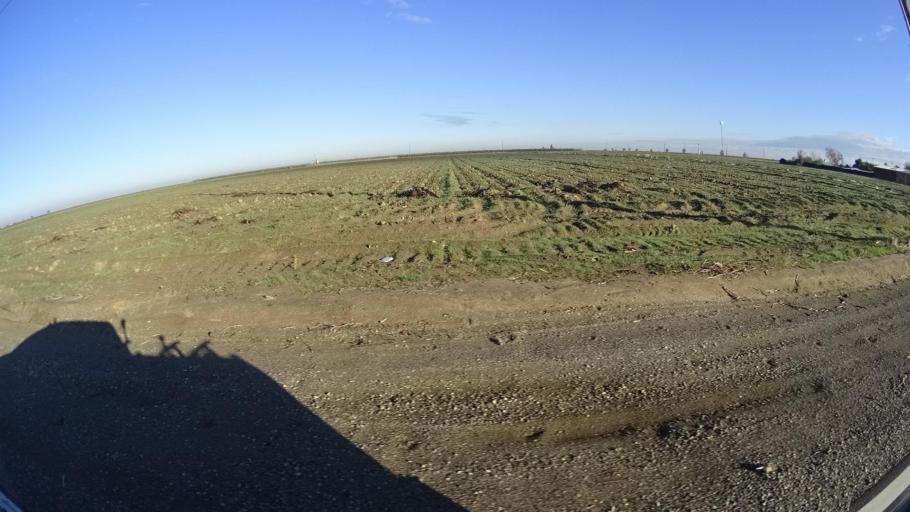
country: US
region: California
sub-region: Kern County
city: Delano
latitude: 35.7904
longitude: -119.2710
